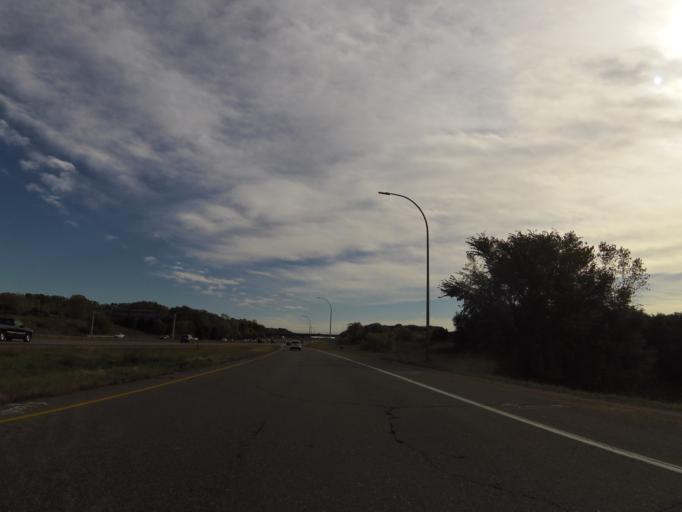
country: US
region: Minnesota
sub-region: Dakota County
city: Mendota Heights
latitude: 44.8622
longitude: -93.1383
